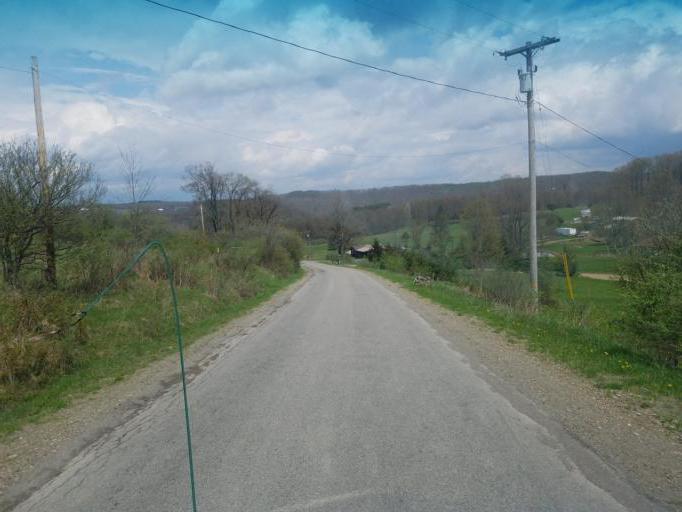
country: US
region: New York
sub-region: Allegany County
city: Andover
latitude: 42.0255
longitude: -77.7604
